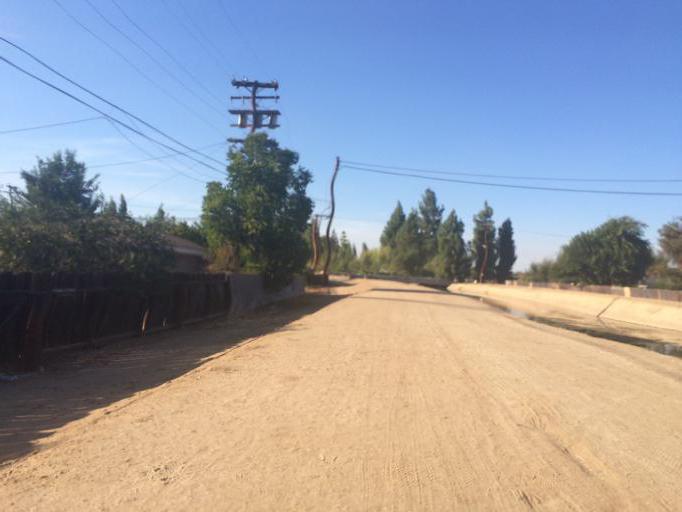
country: US
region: California
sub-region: Fresno County
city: Fresno
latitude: 36.7754
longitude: -119.7639
